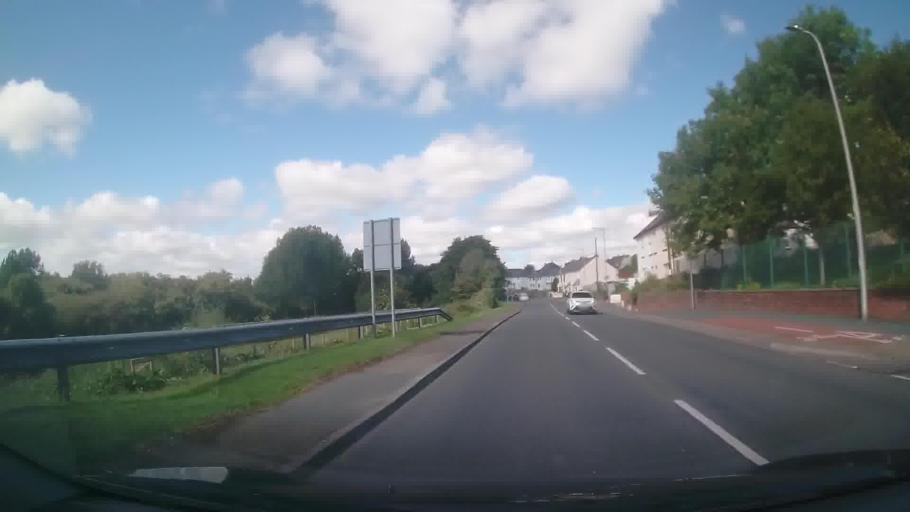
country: GB
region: Wales
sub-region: Pembrokeshire
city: Tenby
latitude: 51.6721
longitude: -4.7143
